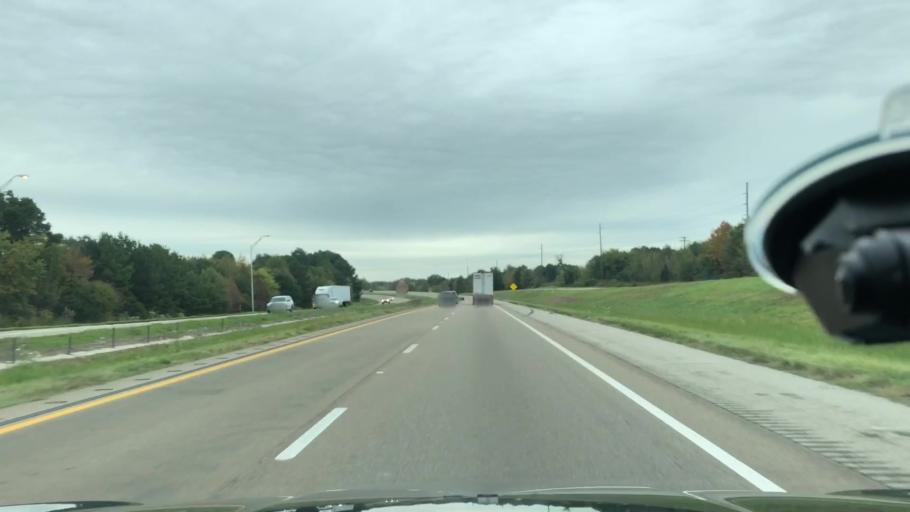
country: US
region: Texas
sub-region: Titus County
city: Mount Pleasant
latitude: 33.1582
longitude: -95.0413
